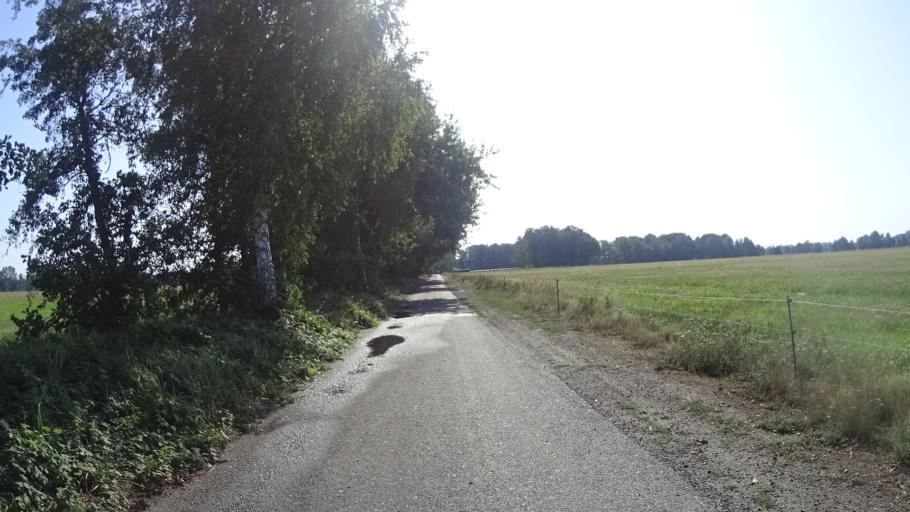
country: DE
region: Brandenburg
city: Straupitz
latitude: 51.8976
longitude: 14.1040
